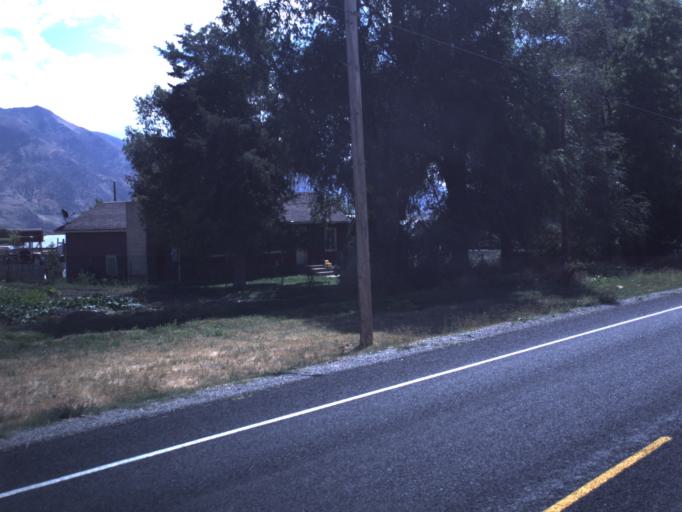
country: US
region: Utah
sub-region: Box Elder County
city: Garland
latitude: 41.7336
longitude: -112.1433
